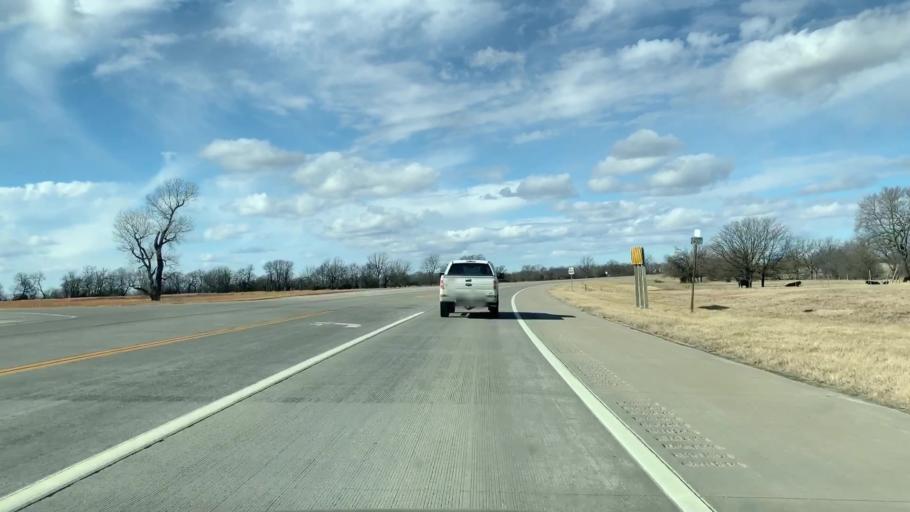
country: US
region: Kansas
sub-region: Labette County
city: Parsons
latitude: 37.3419
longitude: -95.1811
